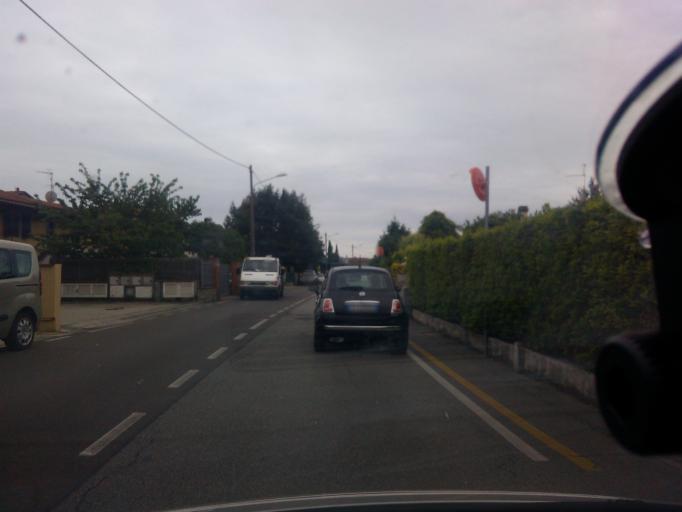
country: IT
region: Tuscany
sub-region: Provincia di Massa-Carrara
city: Massa
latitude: 44.0176
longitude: 10.1123
